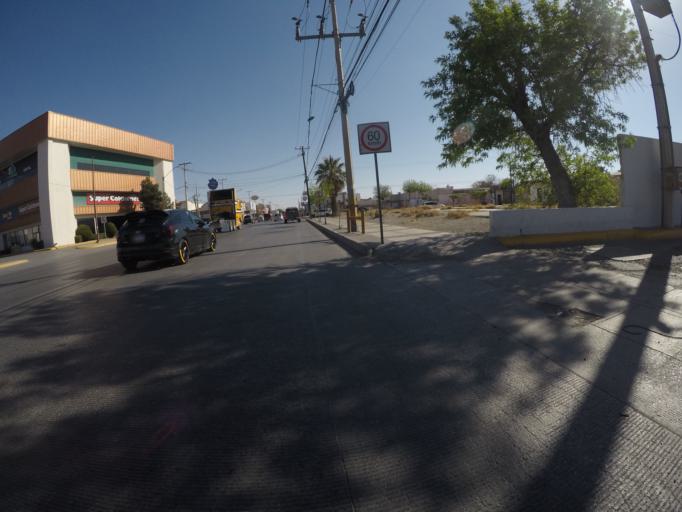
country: MX
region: Chihuahua
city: Ciudad Juarez
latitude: 31.7310
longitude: -106.4502
